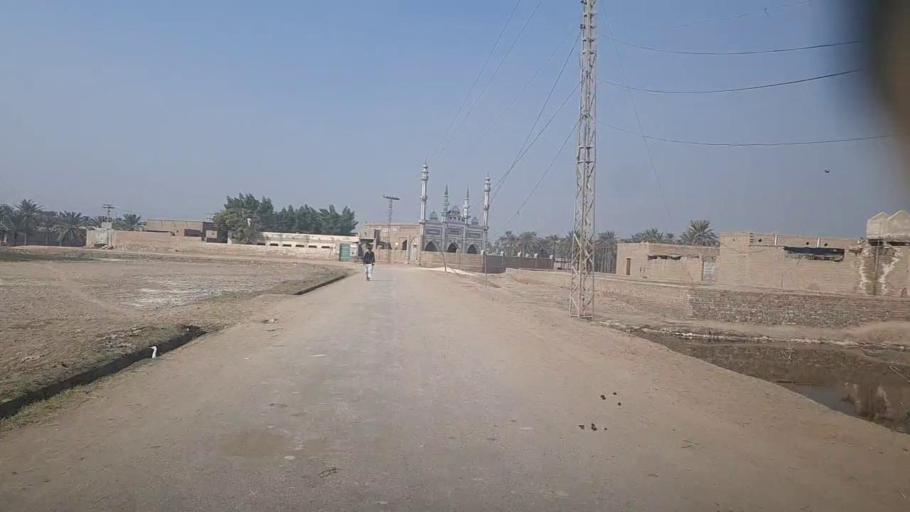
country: PK
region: Sindh
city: Khairpur
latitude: 27.5522
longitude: 68.7825
